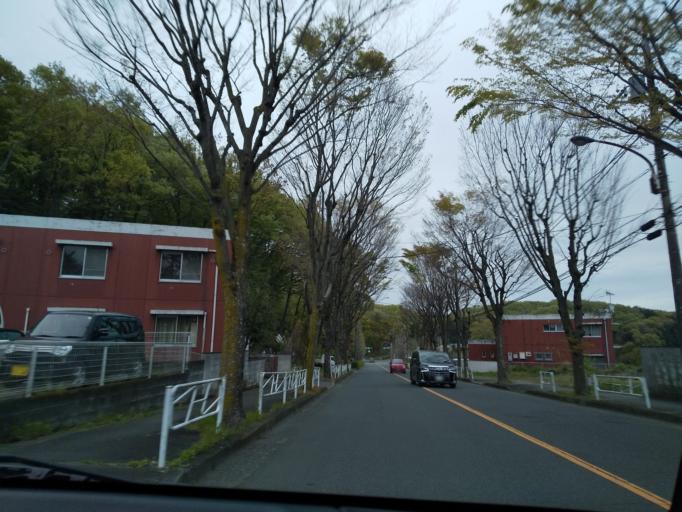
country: JP
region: Tokyo
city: Hino
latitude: 35.6354
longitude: 139.3826
